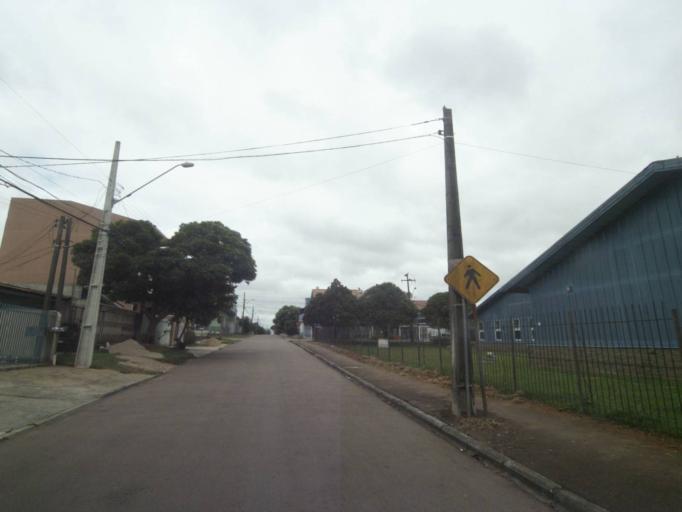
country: BR
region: Parana
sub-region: Sao Jose Dos Pinhais
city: Sao Jose dos Pinhais
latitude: -25.5494
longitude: -49.2616
